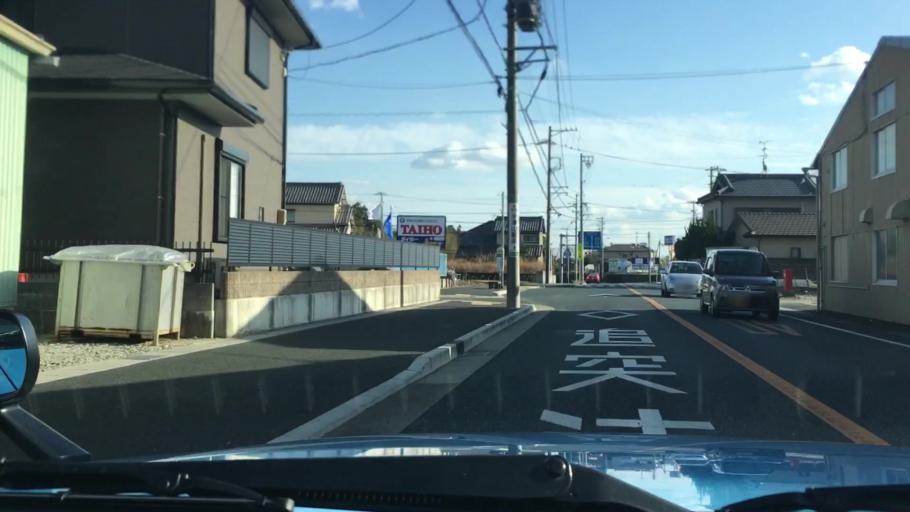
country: JP
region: Shizuoka
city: Hamamatsu
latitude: 34.7533
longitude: 137.6716
